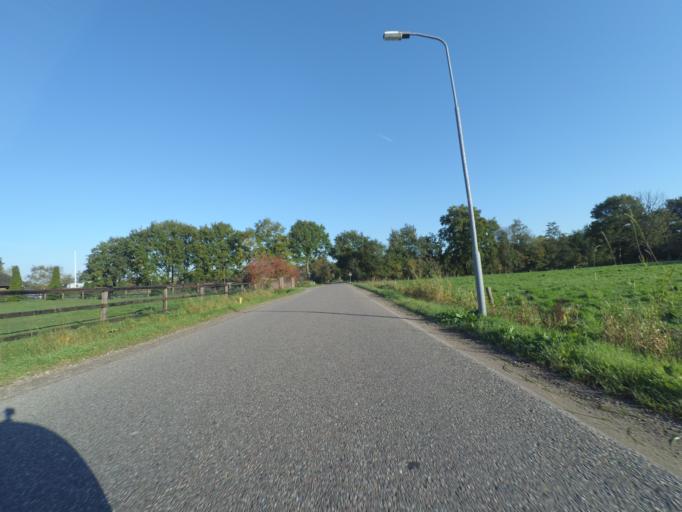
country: NL
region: Gelderland
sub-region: Gemeente Barneveld
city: Zwartebroek
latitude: 52.2032
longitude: 5.5425
